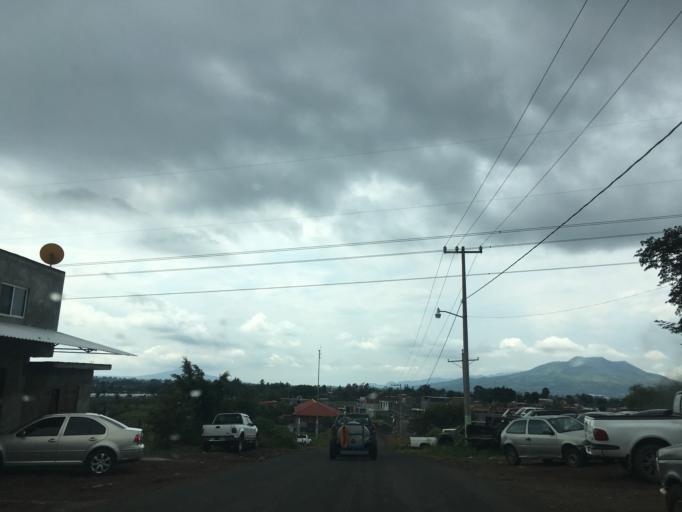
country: MX
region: Michoacan
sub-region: Periban
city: Gildardo Magana (Los Angeles)
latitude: 19.5793
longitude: -102.4517
